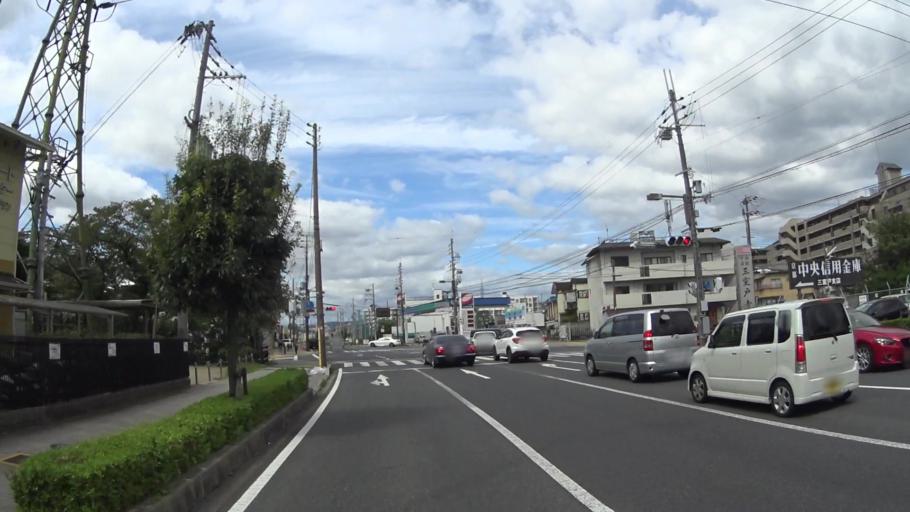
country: JP
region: Kyoto
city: Uji
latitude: 34.8980
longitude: 135.8092
